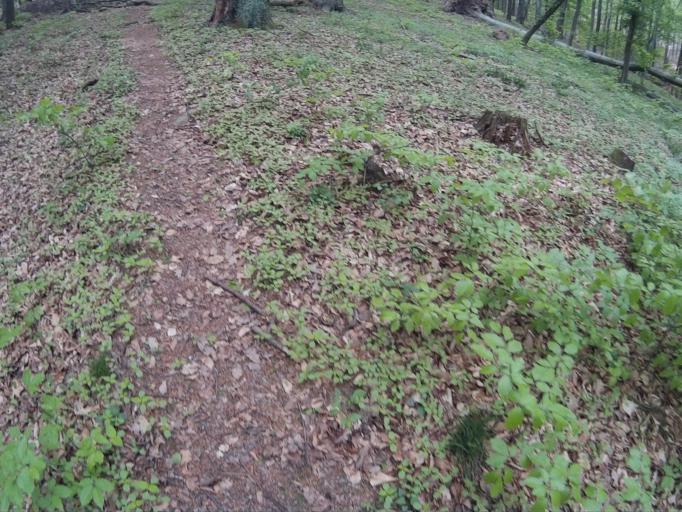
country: HU
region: Vas
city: Koszeg
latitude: 47.3579
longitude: 16.4891
